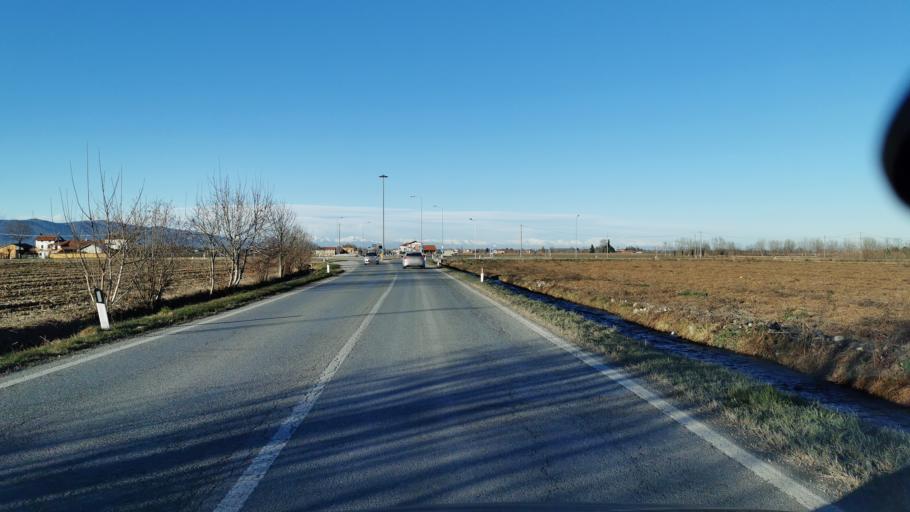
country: IT
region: Piedmont
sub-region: Provincia di Cuneo
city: Roata Rossi
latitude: 44.4379
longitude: 7.5437
